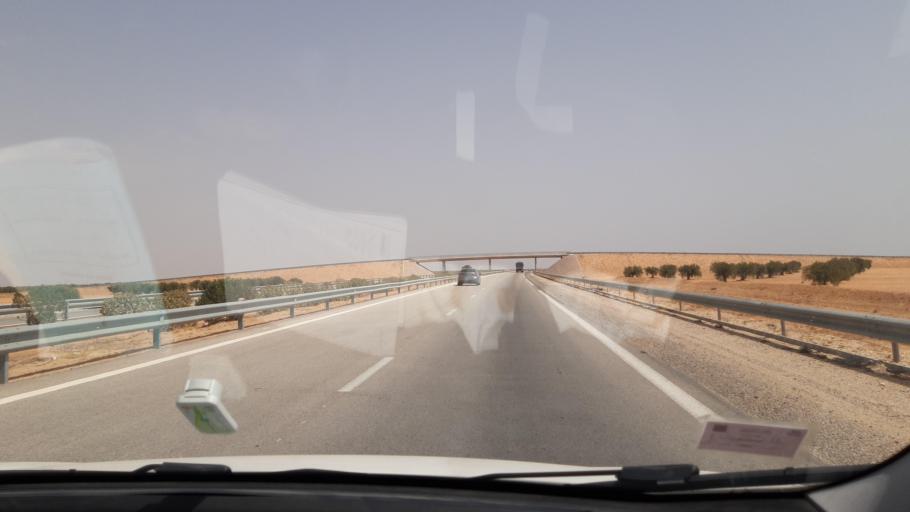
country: TN
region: Safaqis
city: Bi'r `Ali Bin Khalifah
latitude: 34.5286
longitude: 10.1188
